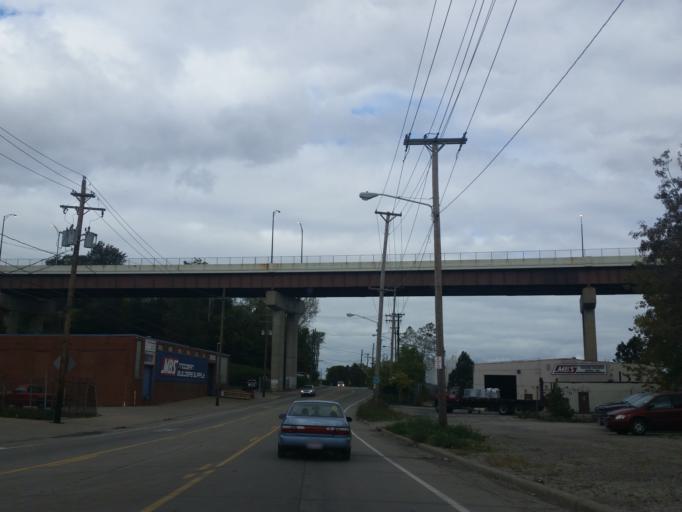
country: US
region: Ohio
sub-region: Cuyahoga County
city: Newburgh Heights
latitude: 41.4505
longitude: -81.6878
